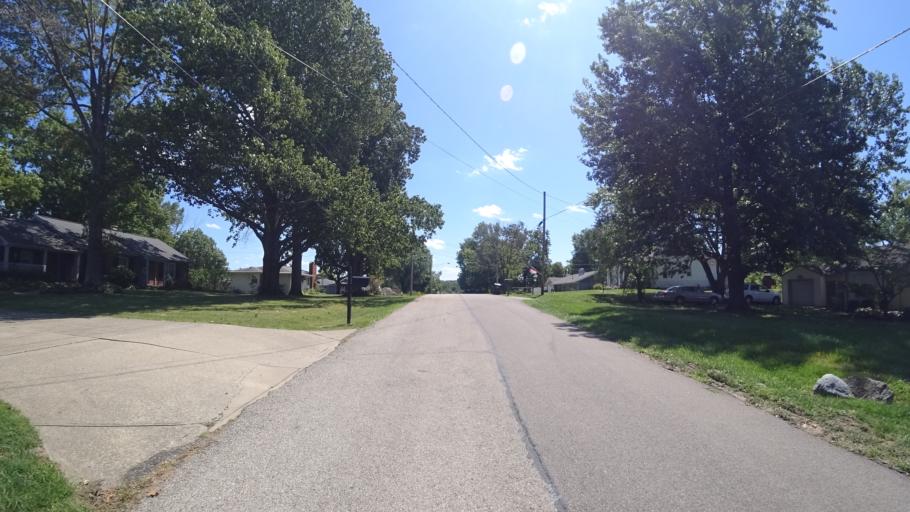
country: US
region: Ohio
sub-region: Butler County
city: New Miami
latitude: 39.4071
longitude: -84.5282
